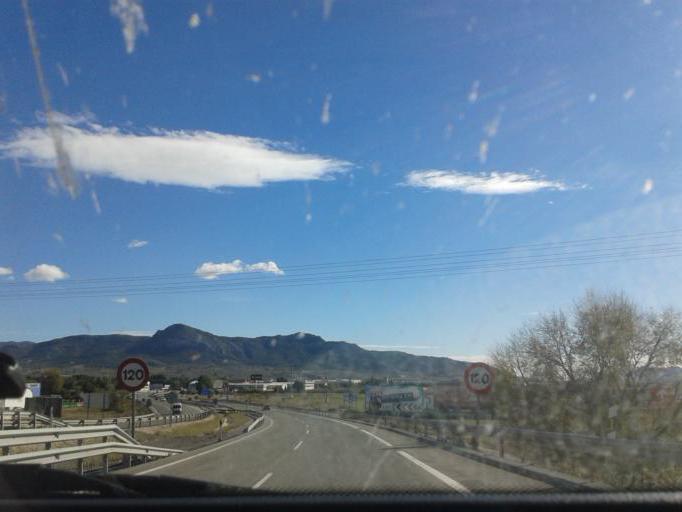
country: ES
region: Valencia
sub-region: Provincia de Alicante
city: Villena
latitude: 38.6281
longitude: -0.8574
